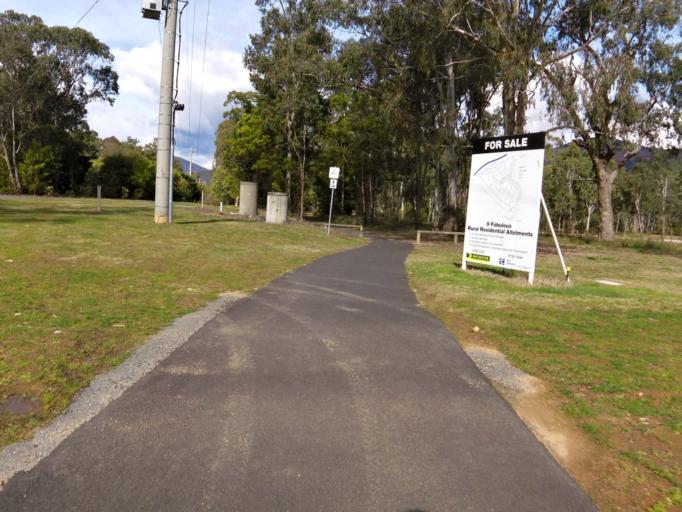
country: AU
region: Victoria
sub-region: Alpine
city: Mount Beauty
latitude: -36.7159
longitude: 146.9426
